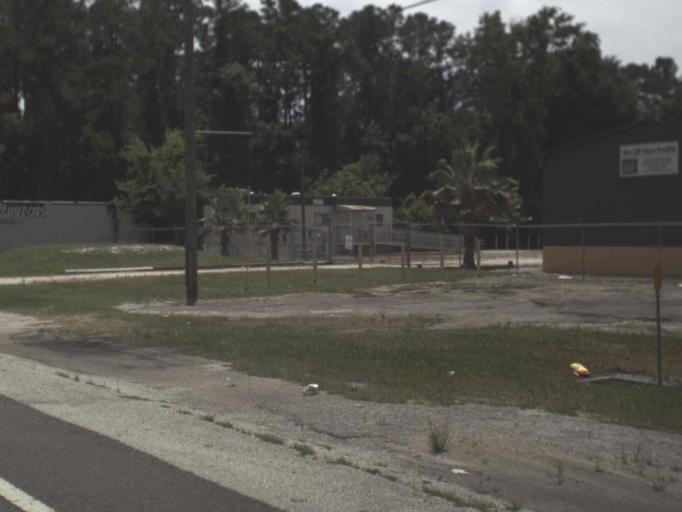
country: US
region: Florida
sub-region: Duval County
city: Jacksonville
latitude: 30.4029
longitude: -81.7424
